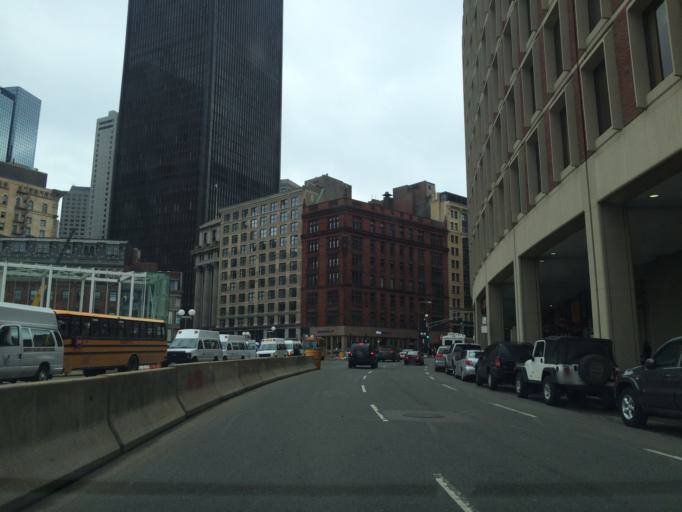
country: US
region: Massachusetts
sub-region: Suffolk County
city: Boston
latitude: 42.3602
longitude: -71.0602
